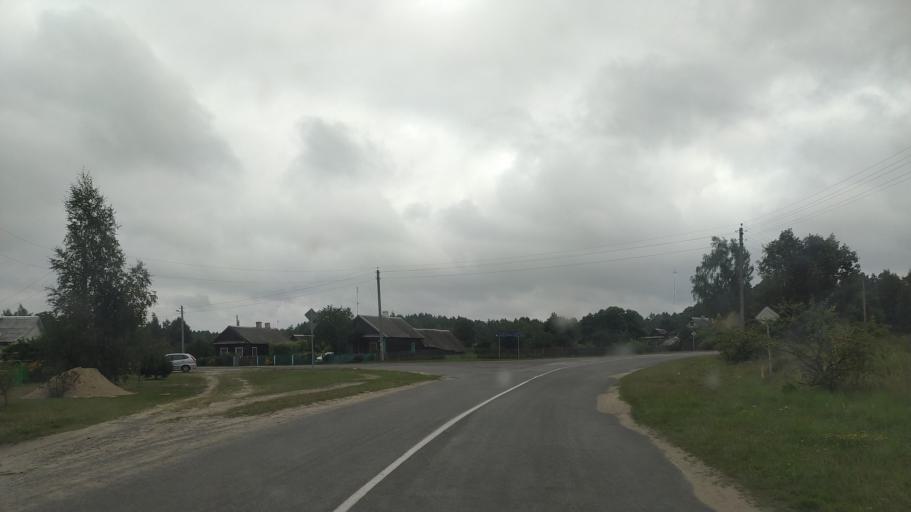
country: BY
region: Brest
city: Byaroza
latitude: 52.5951
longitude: 24.8708
